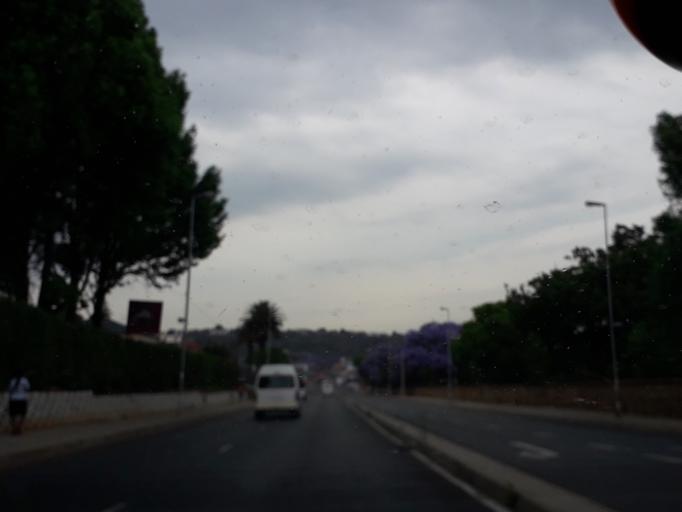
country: ZA
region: Gauteng
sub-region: City of Johannesburg Metropolitan Municipality
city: Johannesburg
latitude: -26.1523
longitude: 28.0863
